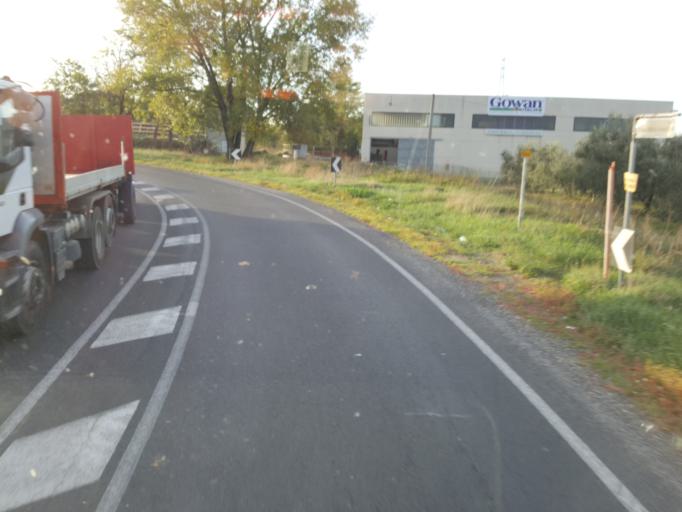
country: IT
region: Emilia-Romagna
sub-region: Provincia di Ravenna
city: Faenza
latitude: 44.3024
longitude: 11.8714
